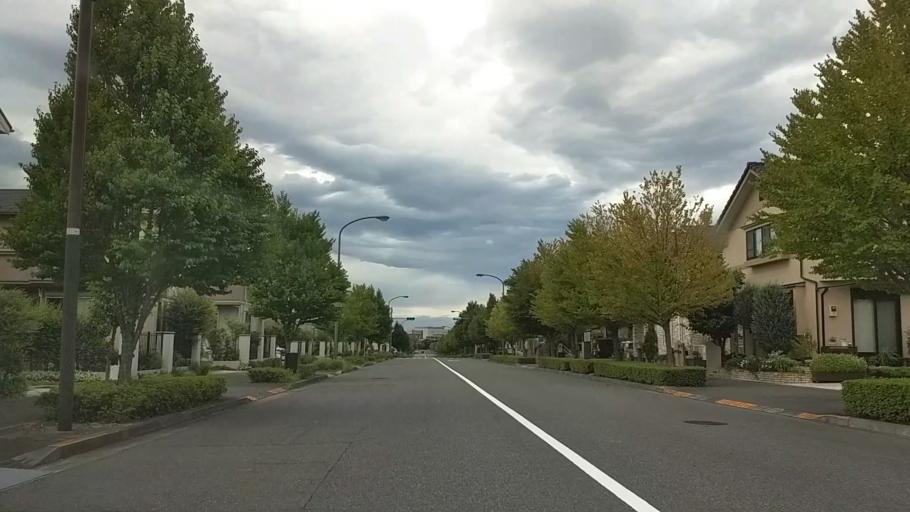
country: JP
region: Tokyo
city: Hachioji
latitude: 35.6197
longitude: 139.3193
